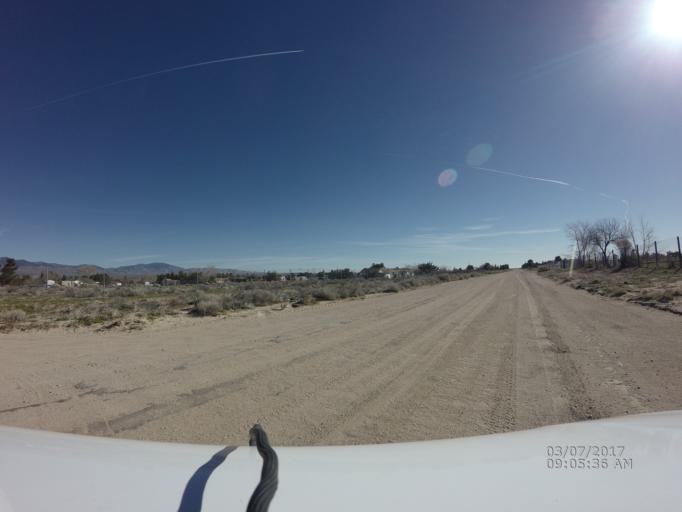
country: US
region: California
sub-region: Los Angeles County
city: Green Valley
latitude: 34.7964
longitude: -118.5808
